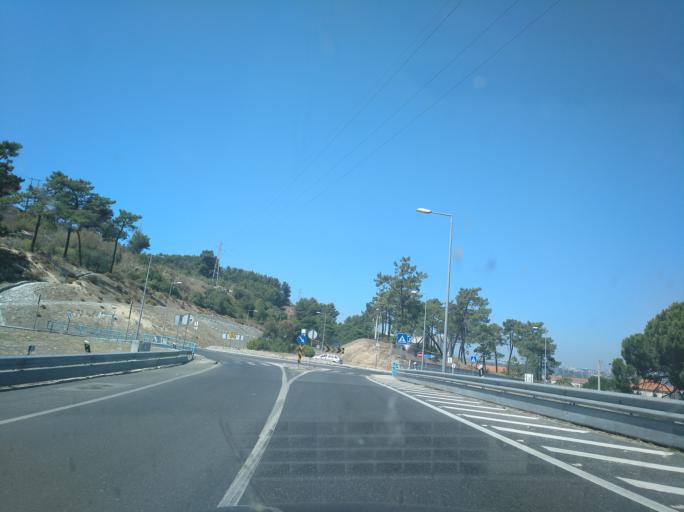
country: PT
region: Setubal
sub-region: Almada
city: Trafaria
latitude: 38.6662
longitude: -9.2308
